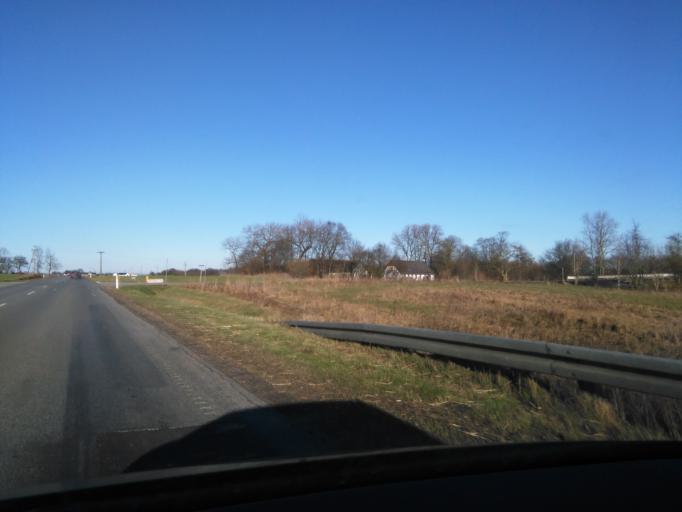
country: DK
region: North Denmark
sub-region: Mariagerfjord Kommune
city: Hobro
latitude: 56.6675
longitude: 9.8081
